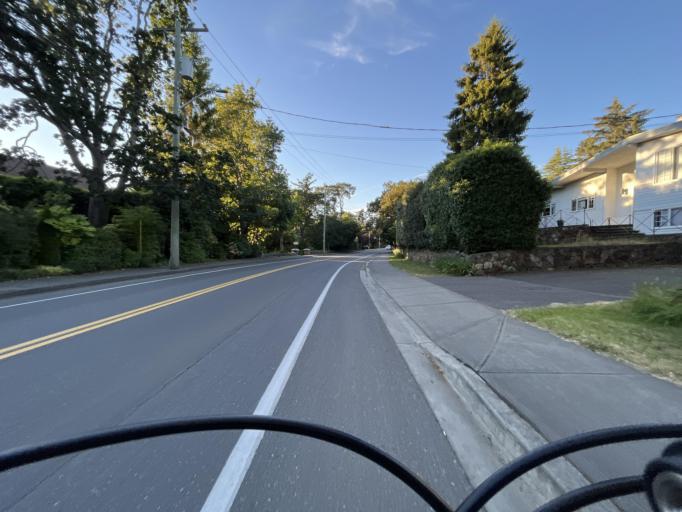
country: CA
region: British Columbia
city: Oak Bay
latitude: 48.4170
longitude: -123.3275
